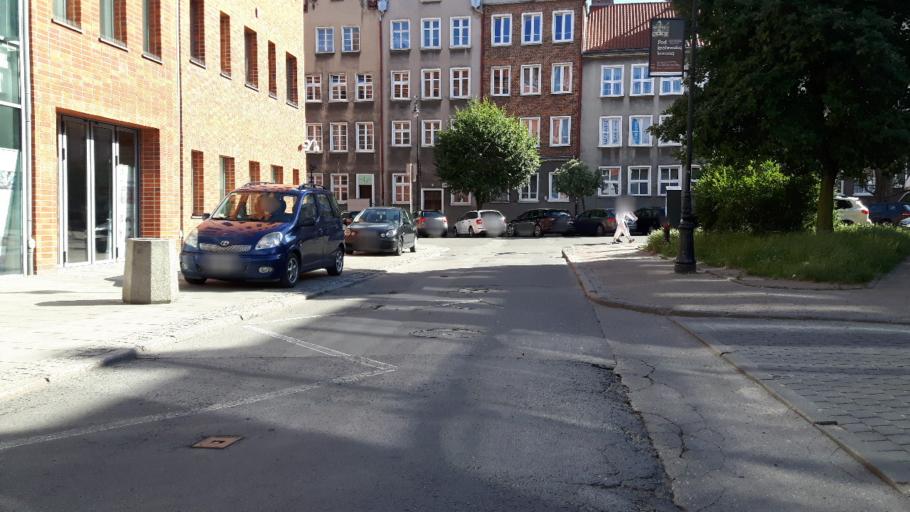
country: PL
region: Pomeranian Voivodeship
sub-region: Gdansk
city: Gdansk
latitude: 54.3509
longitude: 18.6571
